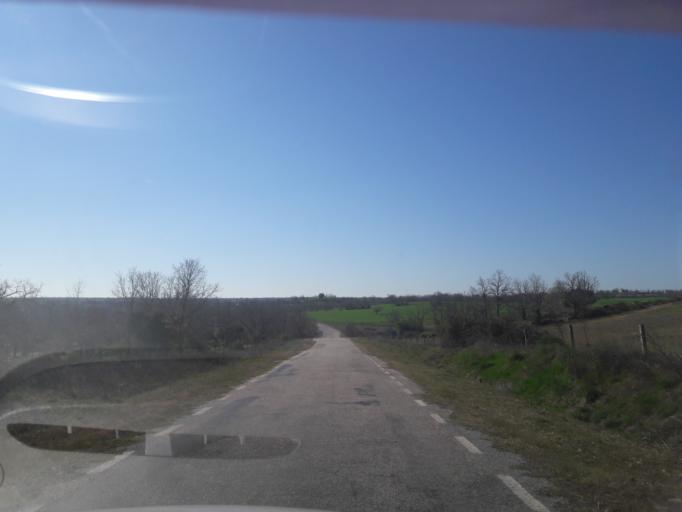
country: ES
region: Castille and Leon
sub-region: Provincia de Salamanca
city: Valsalabroso
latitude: 41.1629
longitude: -6.4971
